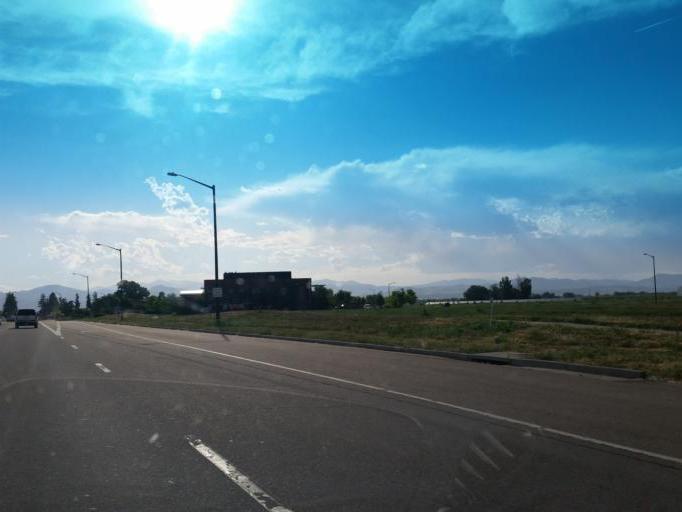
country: US
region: Colorado
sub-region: Larimer County
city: Loveland
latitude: 40.4075
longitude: -105.0242
